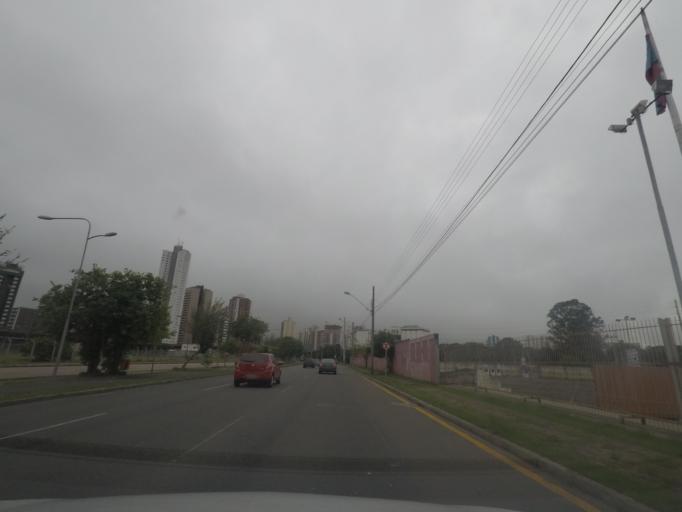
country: BR
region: Parana
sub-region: Curitiba
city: Curitiba
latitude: -25.4382
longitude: -49.2560
